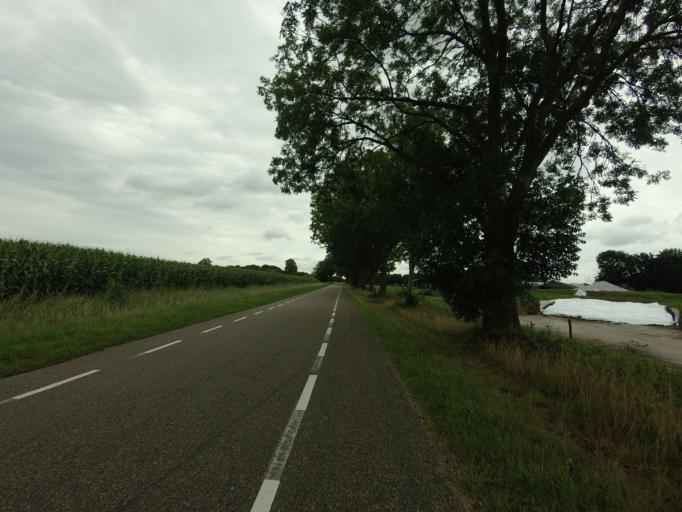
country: NL
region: Gelderland
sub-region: Gemeente Lochem
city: Laren
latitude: 52.2912
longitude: 6.3520
